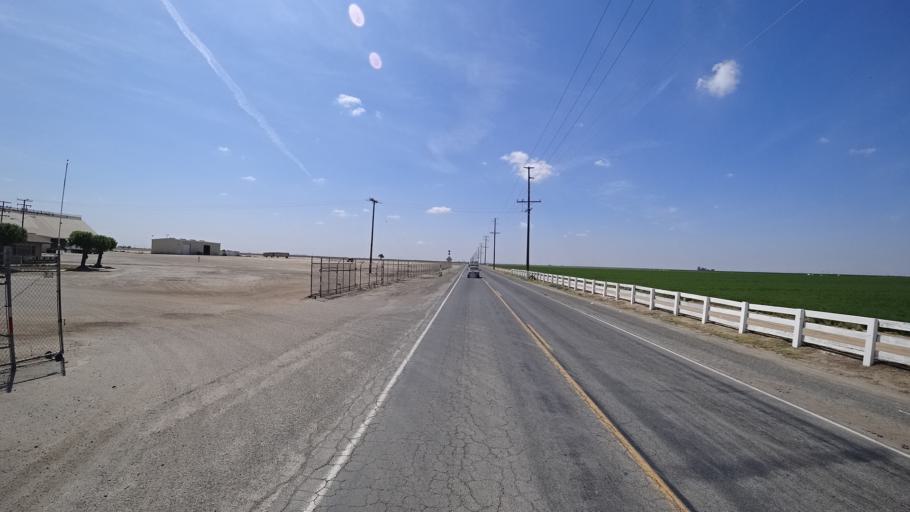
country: US
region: California
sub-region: Tulare County
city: Goshen
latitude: 36.2966
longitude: -119.4921
